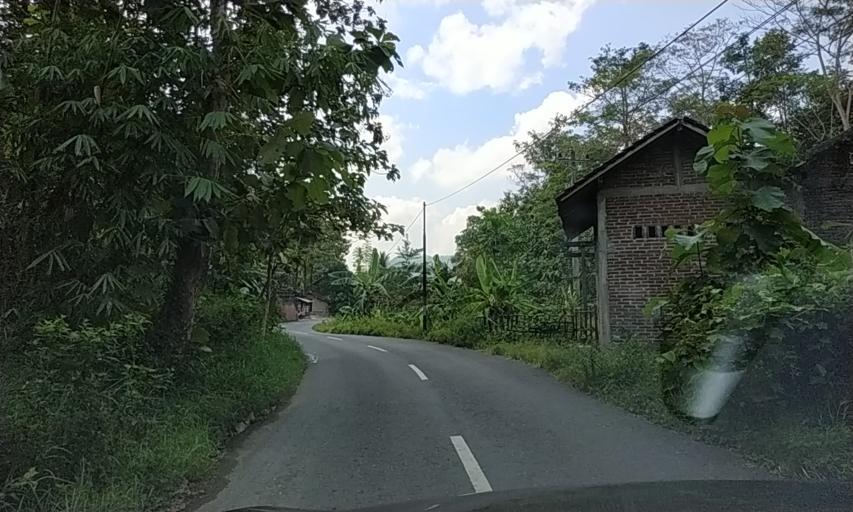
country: ID
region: Central Java
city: Gombong
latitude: -7.6328
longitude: 109.7136
